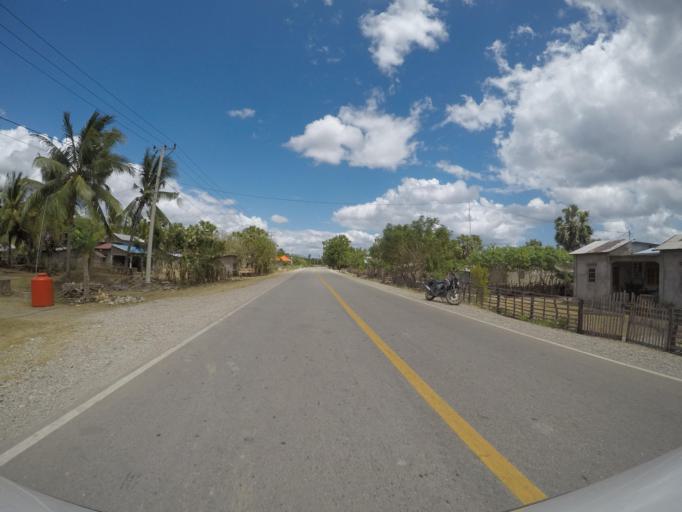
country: TL
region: Lautem
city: Lospalos
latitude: -8.3761
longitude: 126.8718
